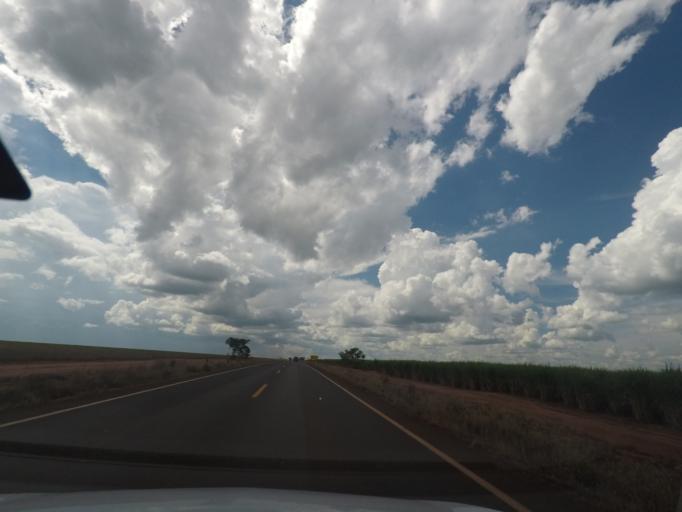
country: BR
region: Minas Gerais
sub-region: Conceicao Das Alagoas
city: Conceicao das Alagoas
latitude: -19.7939
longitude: -48.5837
